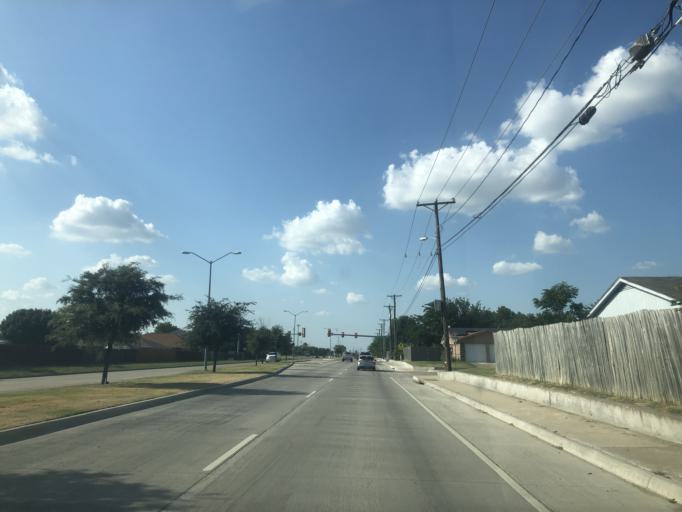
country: US
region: Texas
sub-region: Tarrant County
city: Saginaw
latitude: 32.8735
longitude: -97.3907
